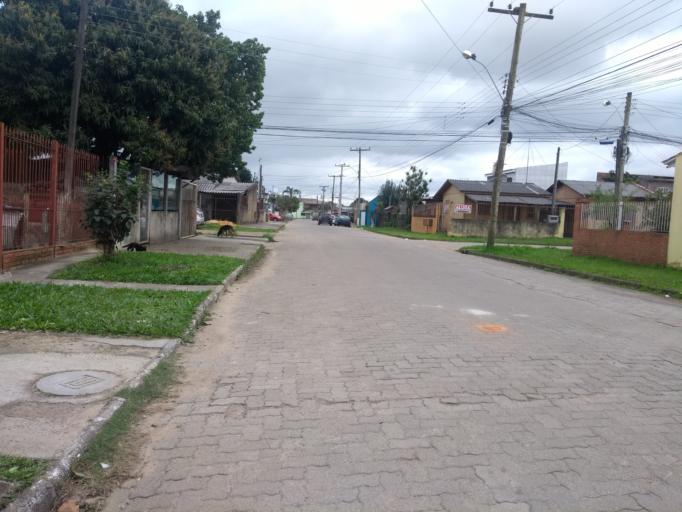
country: BR
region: Rio Grande do Sul
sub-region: Cachoeirinha
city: Cachoeirinha
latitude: -30.0026
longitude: -51.0746
